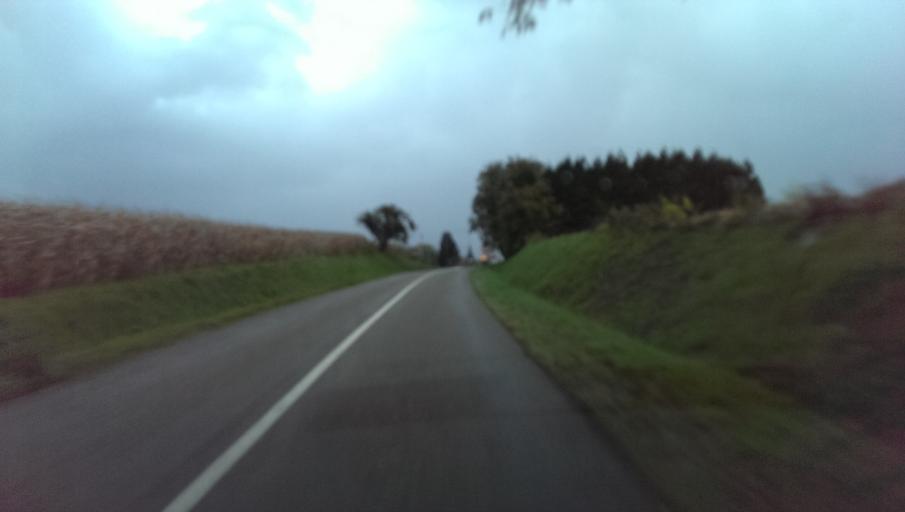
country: FR
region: Alsace
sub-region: Departement du Bas-Rhin
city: Seltz
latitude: 48.9378
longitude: 8.1055
